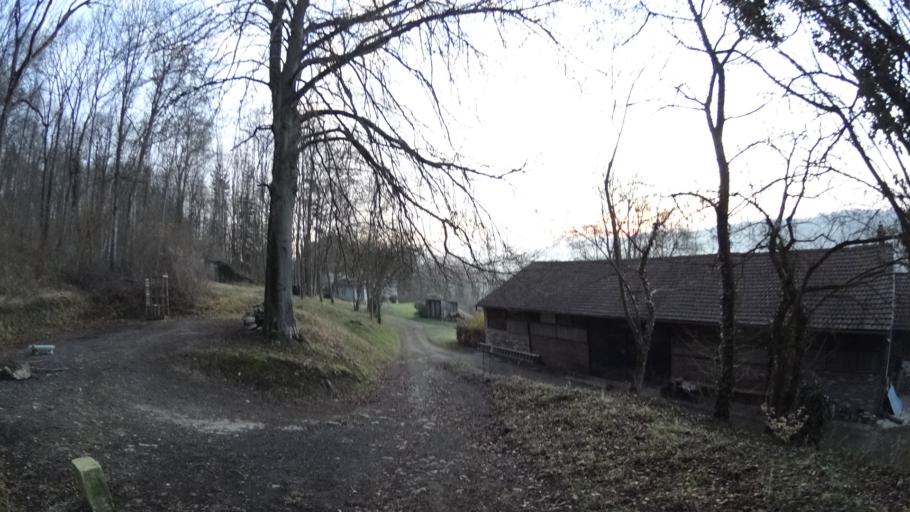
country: FR
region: Picardie
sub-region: Departement de l'Aisne
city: Vic-sur-Aisne
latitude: 49.4371
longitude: 3.1285
